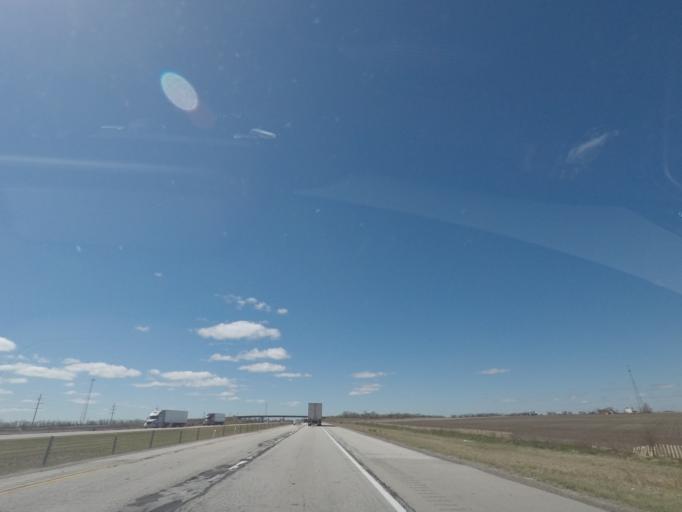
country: US
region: Illinois
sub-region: Livingston County
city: Dwight
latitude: 41.0693
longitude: -88.4584
